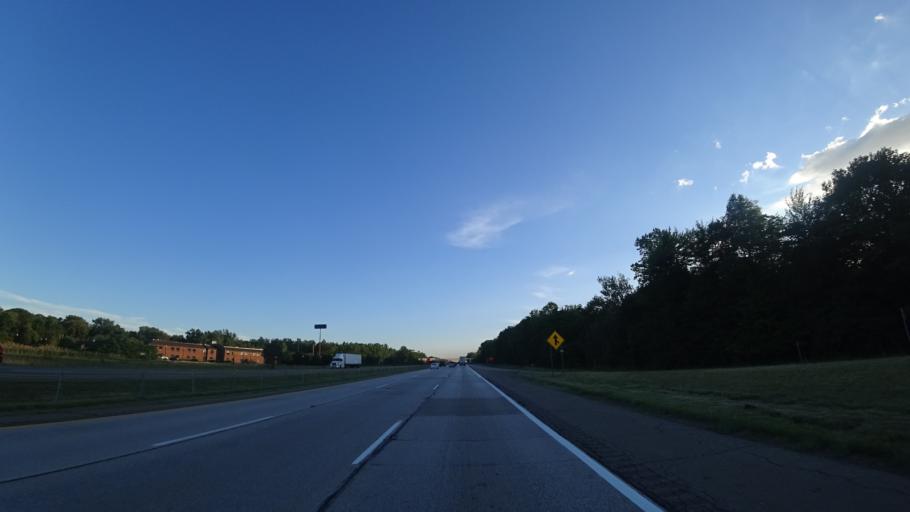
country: US
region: Michigan
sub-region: Berrien County
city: New Buffalo
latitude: 41.7735
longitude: -86.7326
